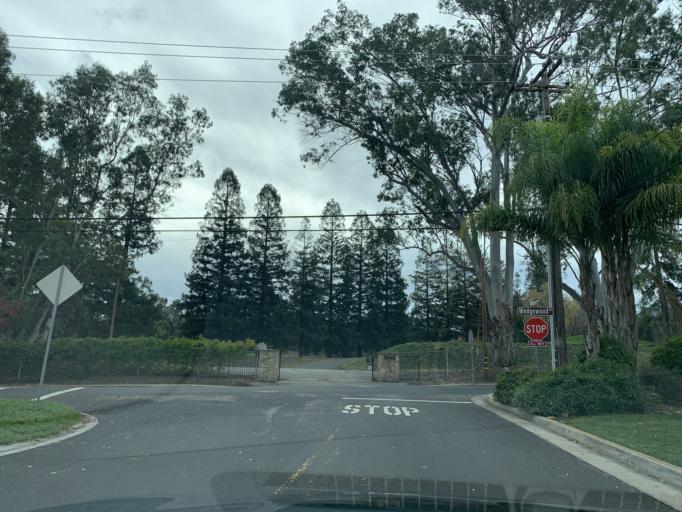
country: US
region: California
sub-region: Santa Clara County
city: Monte Sereno
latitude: 37.2599
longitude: -121.9752
